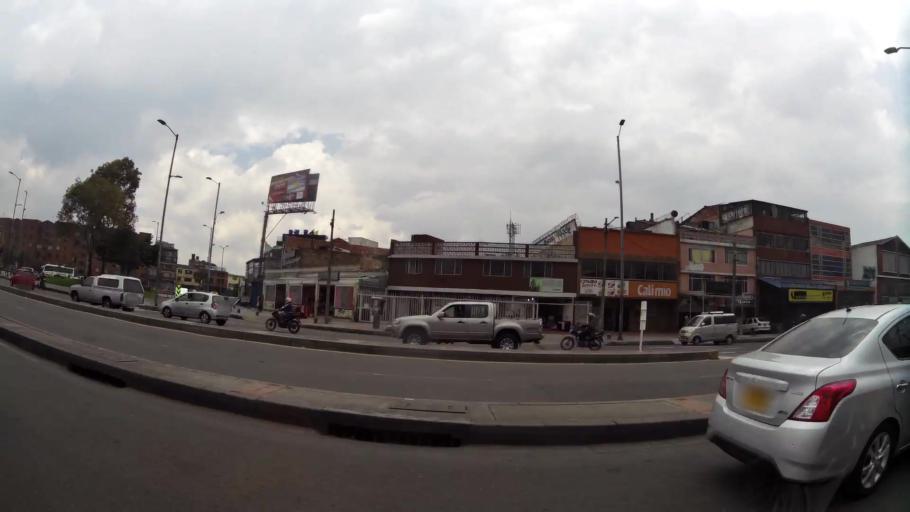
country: CO
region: Bogota D.C.
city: Bogota
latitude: 4.5970
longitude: -74.1139
